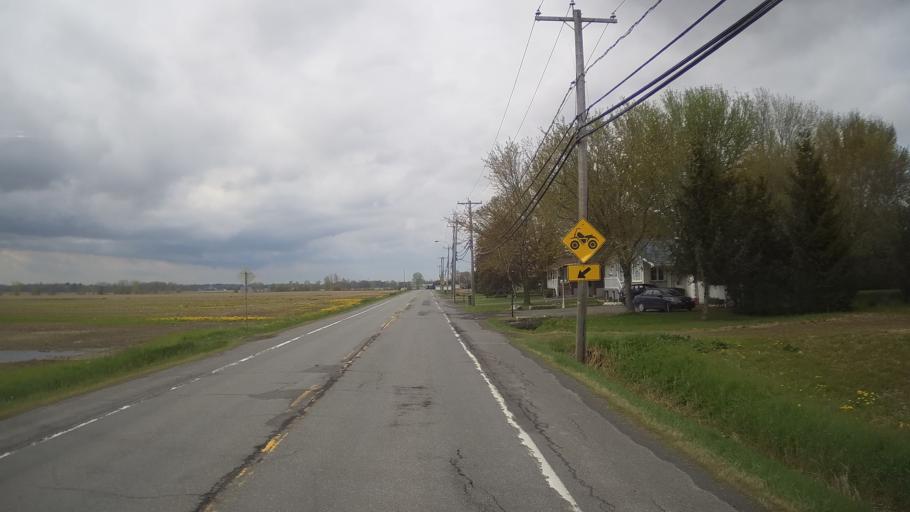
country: CA
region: Quebec
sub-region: Monteregie
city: Saint-Jean-sur-Richelieu
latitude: 45.3325
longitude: -73.1698
